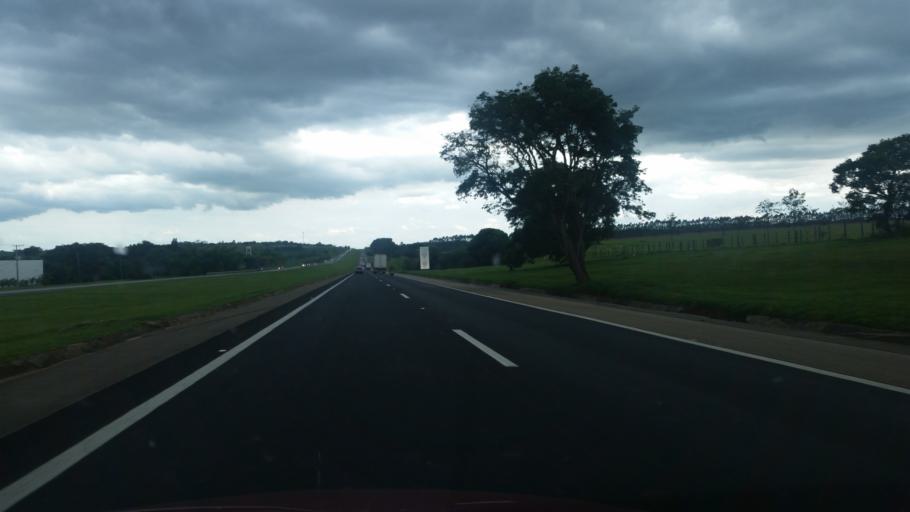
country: BR
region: Sao Paulo
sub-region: Boituva
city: Boituva
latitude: -23.3246
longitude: -47.5713
